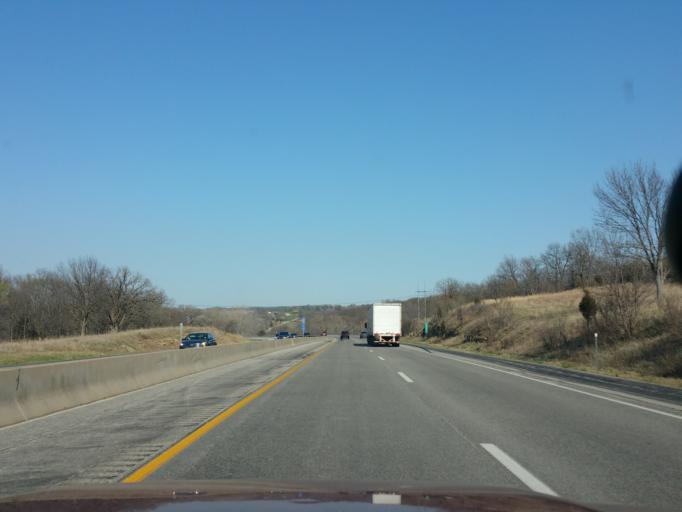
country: US
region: Kansas
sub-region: Wyandotte County
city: Bonner Springs
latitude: 39.0842
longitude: -94.9334
